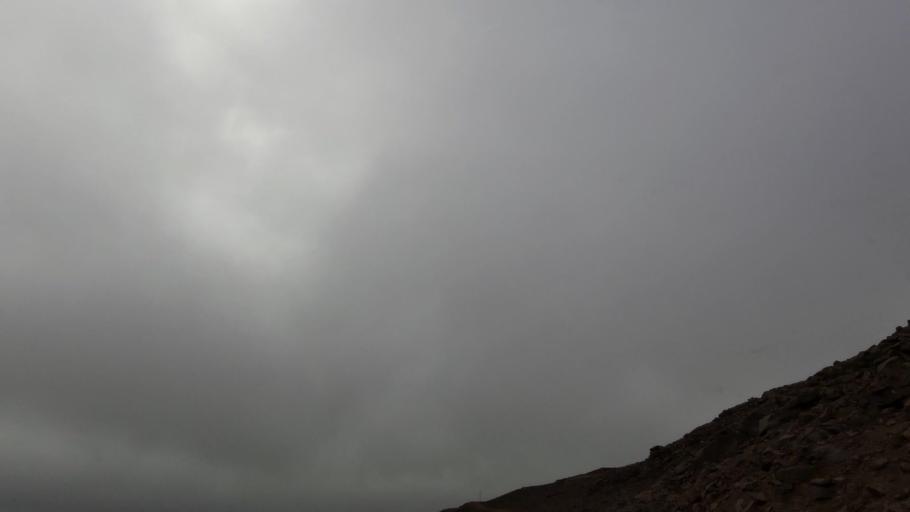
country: IS
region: West
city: Olafsvik
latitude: 65.5272
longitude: -24.4255
